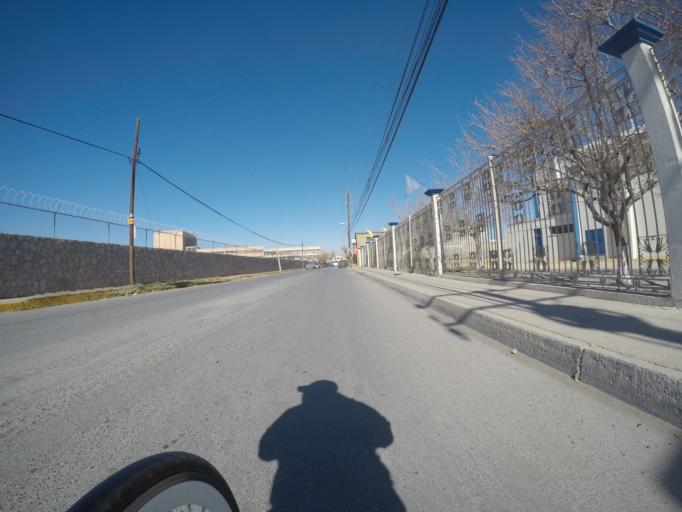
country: MX
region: Chihuahua
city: Ciudad Juarez
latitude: 31.7098
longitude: -106.4131
